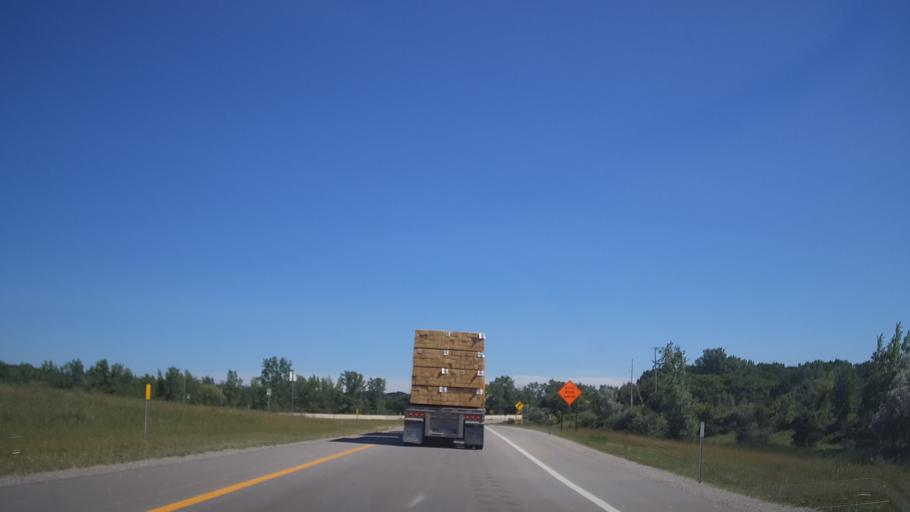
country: US
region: Michigan
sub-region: Bay County
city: Bay City
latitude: 43.5948
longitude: -83.9507
